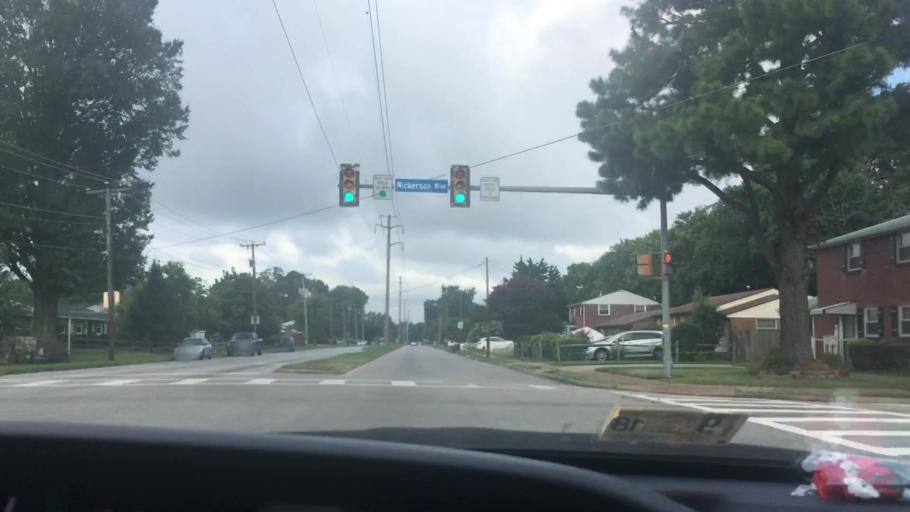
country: US
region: Virginia
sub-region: City of Hampton
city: East Hampton
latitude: 37.0476
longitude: -76.3087
